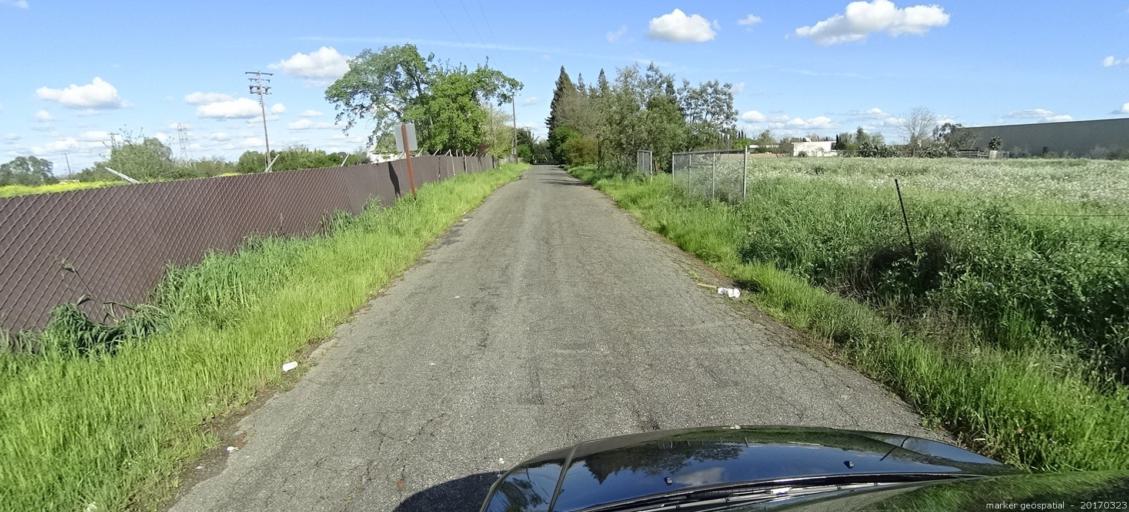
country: US
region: California
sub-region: Sacramento County
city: Rosemont
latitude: 38.5192
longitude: -121.3695
